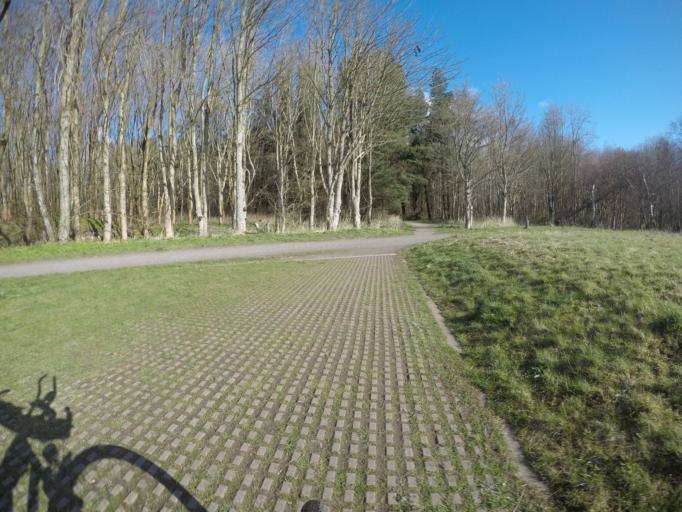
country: GB
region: Scotland
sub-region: North Ayrshire
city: Irvine
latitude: 55.6386
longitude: -4.6568
